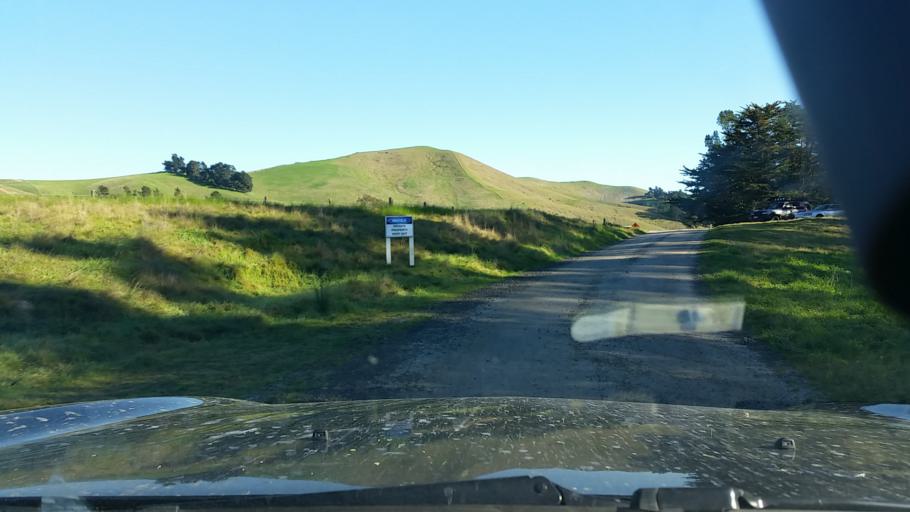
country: NZ
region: Marlborough
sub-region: Marlborough District
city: Blenheim
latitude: -41.5622
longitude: 173.9262
